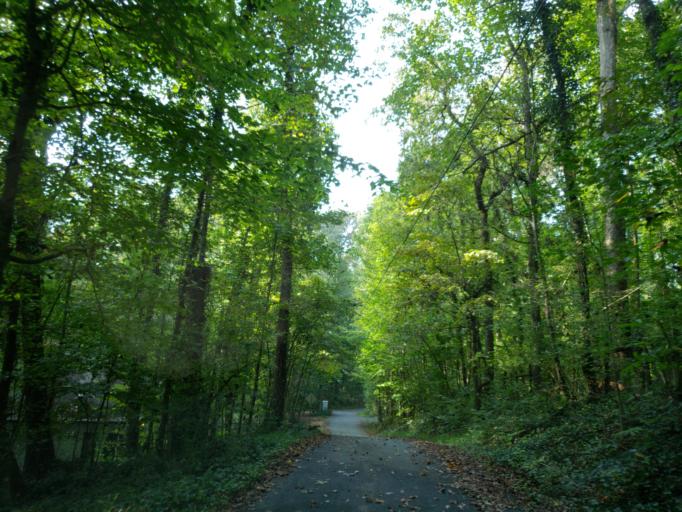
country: US
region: Georgia
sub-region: Fulton County
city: Roswell
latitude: 34.0811
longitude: -84.4133
